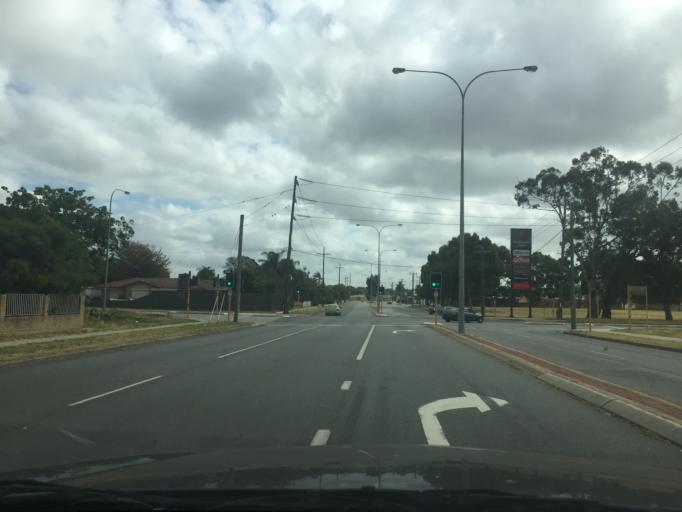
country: AU
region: Western Australia
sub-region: Gosnells
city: Maddington
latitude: -32.0530
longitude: 115.9824
